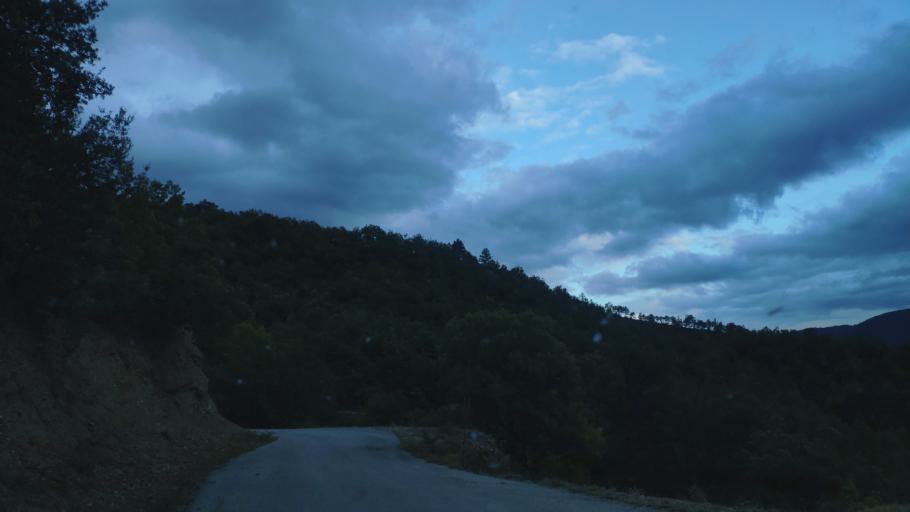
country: AL
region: Korce
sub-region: Rrethi i Kolonjes
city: Erseke
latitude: 40.2517
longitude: 20.8650
